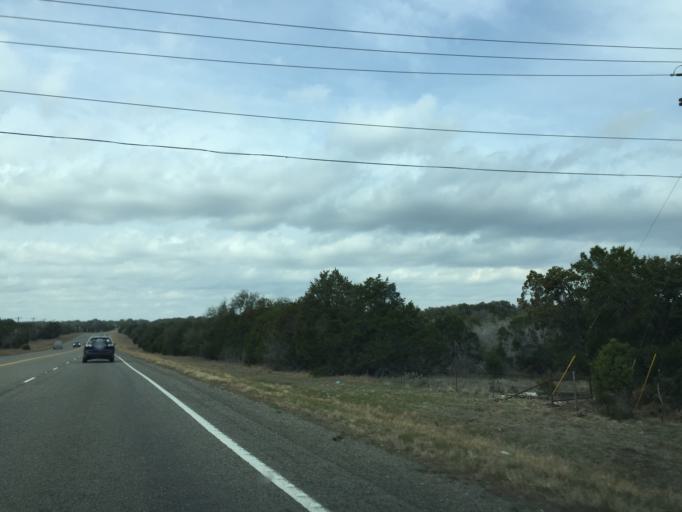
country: US
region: Texas
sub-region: Burnet County
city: Meadowlakes
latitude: 30.4959
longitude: -98.2559
